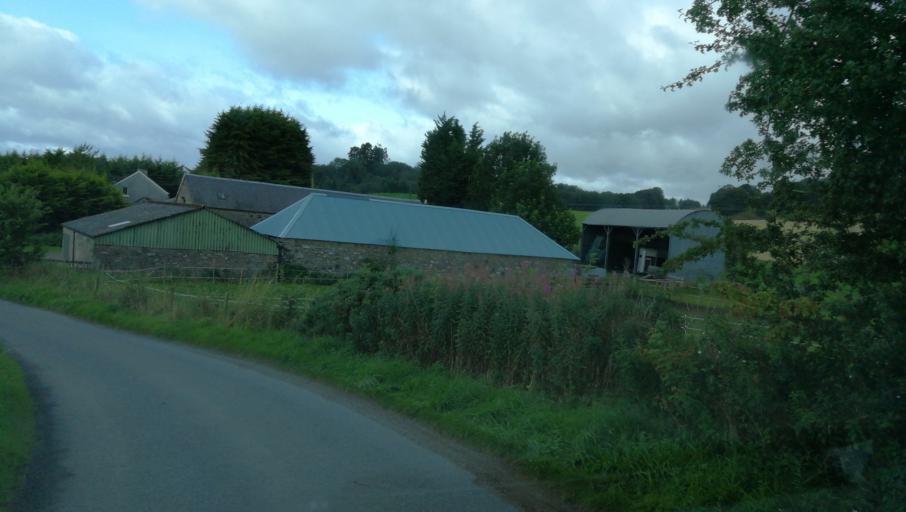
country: GB
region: Scotland
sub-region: Perth and Kinross
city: Blairgowrie
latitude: 56.6040
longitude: -3.3108
